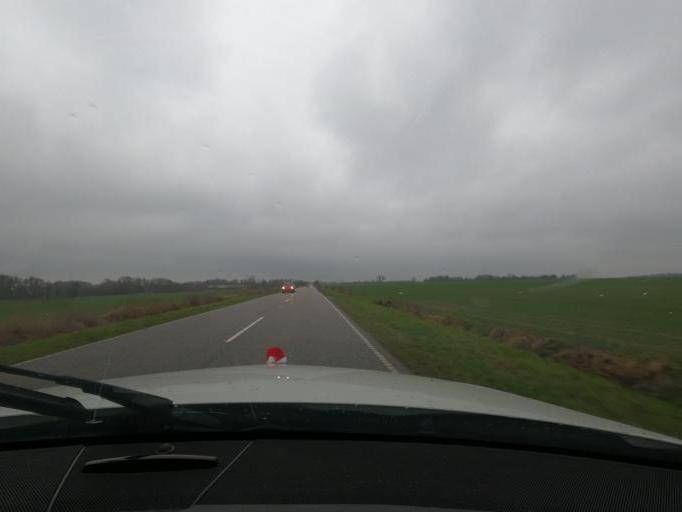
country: DK
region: South Denmark
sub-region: Haderslev Kommune
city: Starup
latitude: 55.2376
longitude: 9.6506
